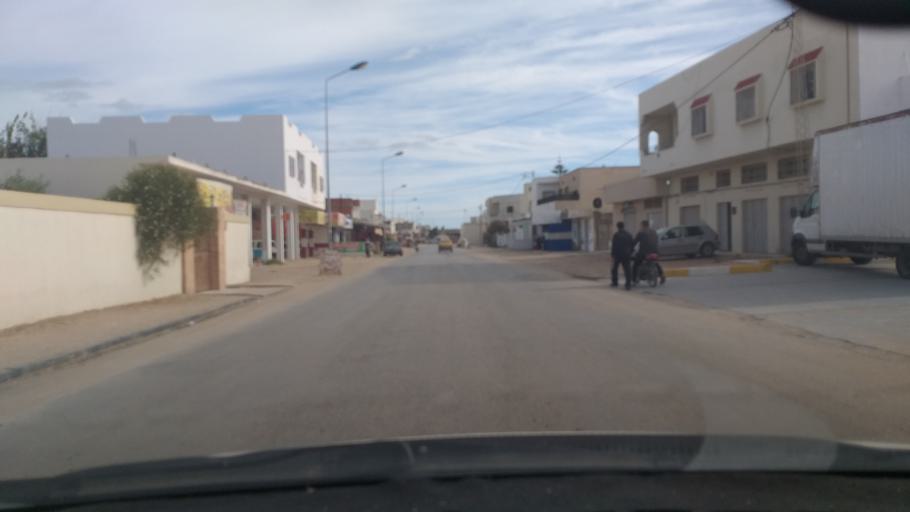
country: TN
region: Safaqis
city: Al Qarmadah
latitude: 34.7954
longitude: 10.8010
